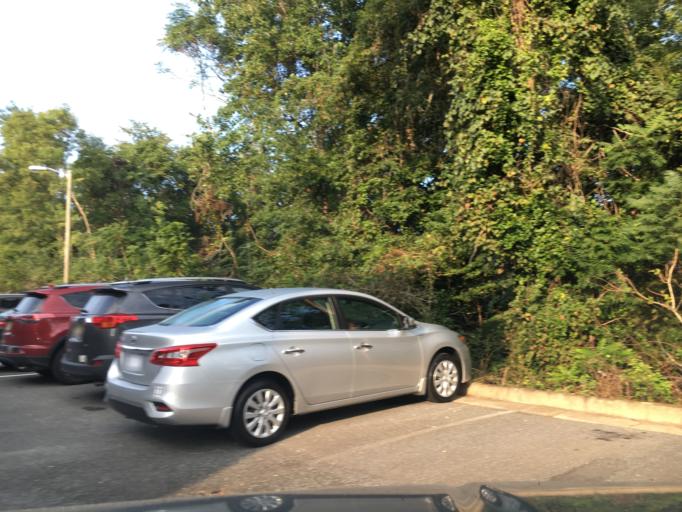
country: US
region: Virginia
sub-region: City of Lynchburg
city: West Lynchburg
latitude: 37.4115
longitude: -79.1744
